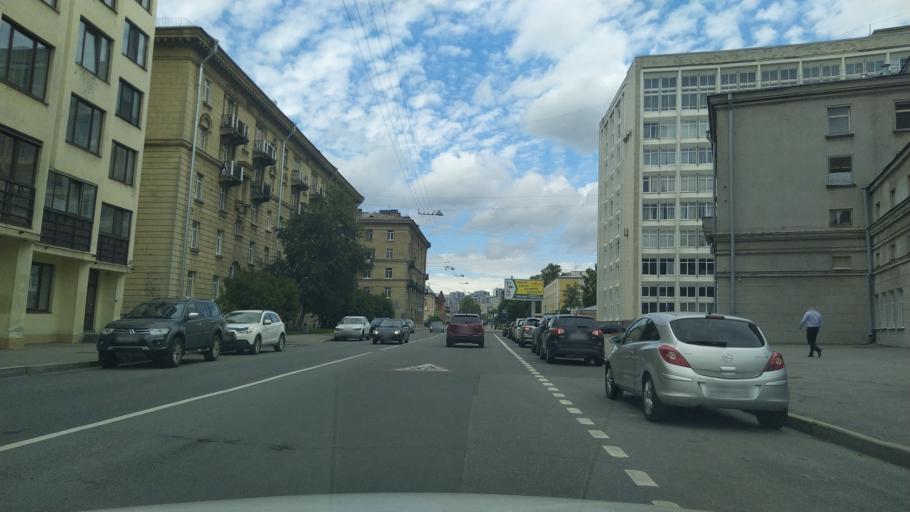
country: RU
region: Leningrad
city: Finlyandskiy
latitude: 59.9708
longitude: 30.3858
